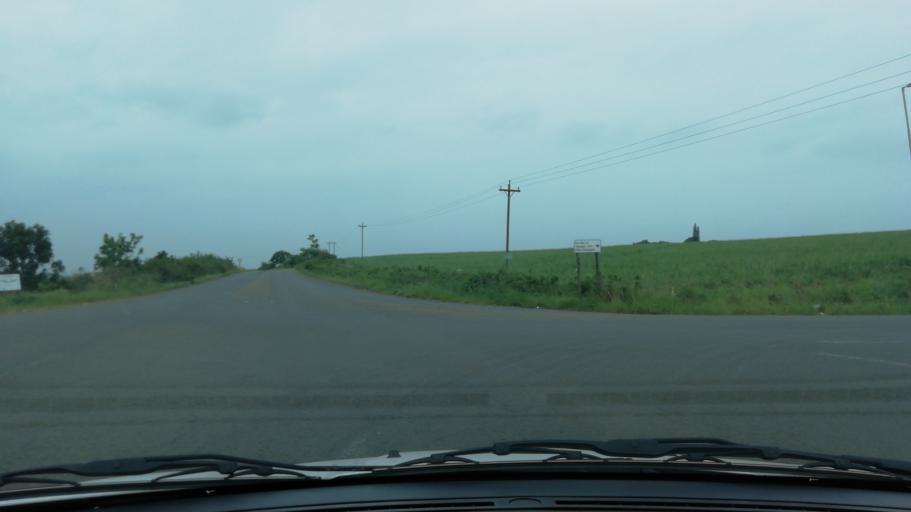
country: ZA
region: KwaZulu-Natal
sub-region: uThungulu District Municipality
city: Empangeni
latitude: -28.7342
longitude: 31.8875
